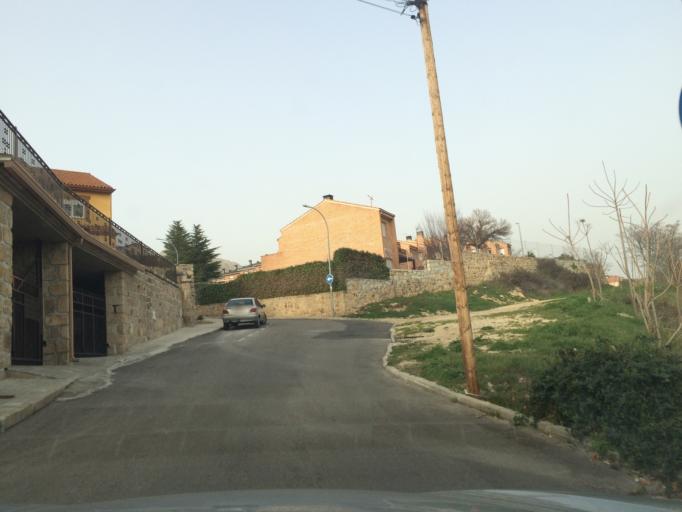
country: ES
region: Madrid
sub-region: Provincia de Madrid
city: Manzanares el Real
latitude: 40.7320
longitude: -3.8634
